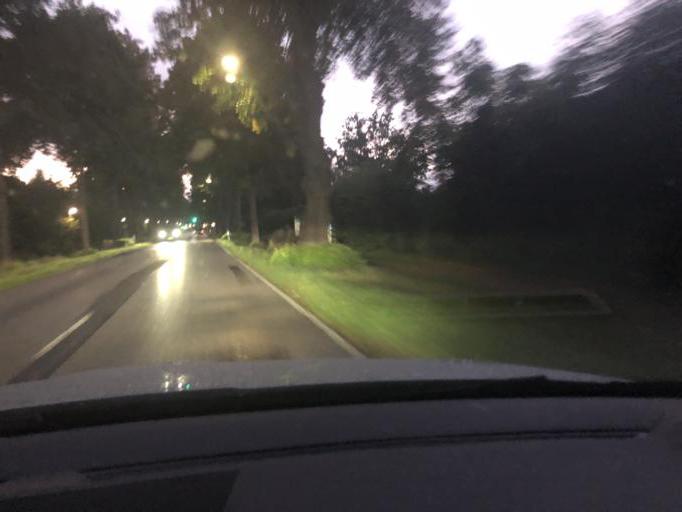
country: DE
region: Schleswig-Holstein
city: Gross Gronau
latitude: 53.8195
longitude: 10.7288
